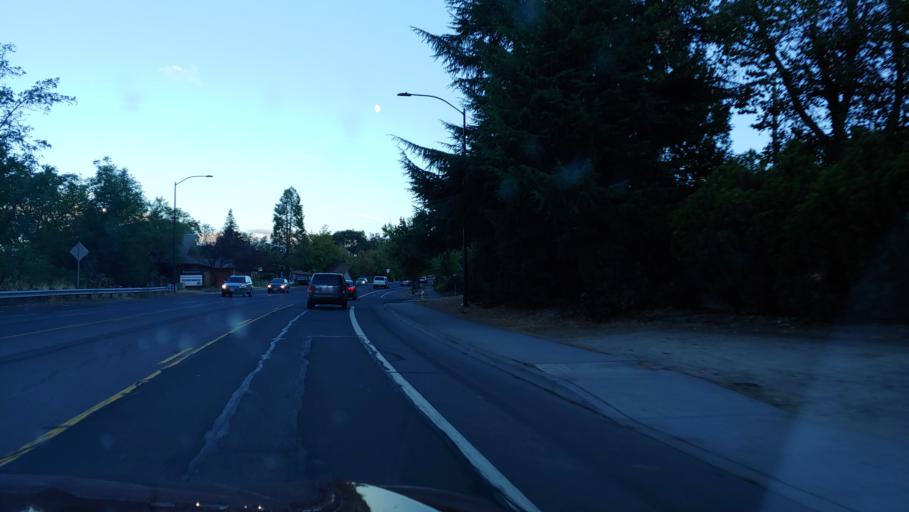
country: US
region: Oregon
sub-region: Jackson County
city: Ashland
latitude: 42.2097
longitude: -122.7245
